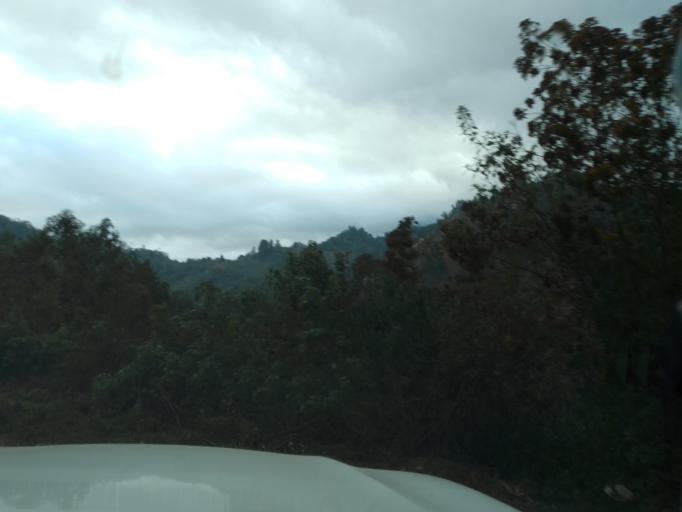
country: GT
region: San Marcos
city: Tacana
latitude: 15.2095
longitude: -92.2171
